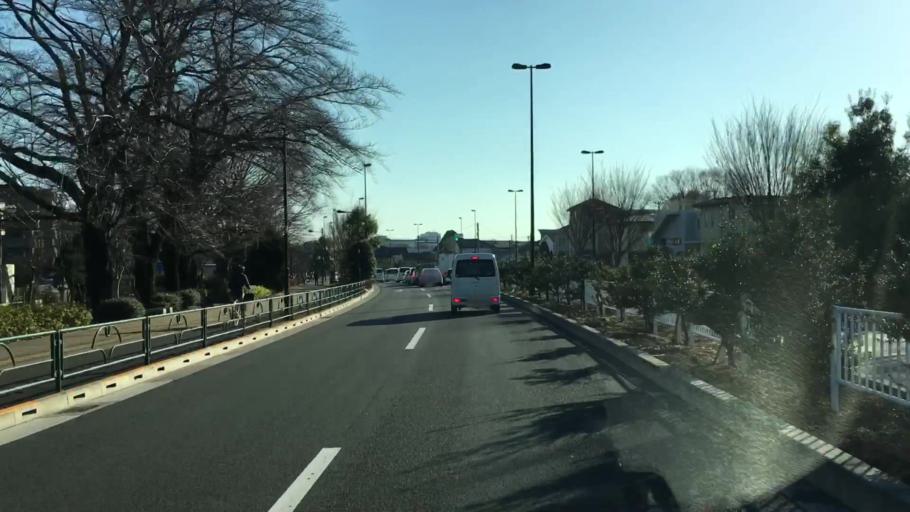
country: JP
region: Tokyo
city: Kamirenjaku
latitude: 35.7054
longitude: 139.5504
